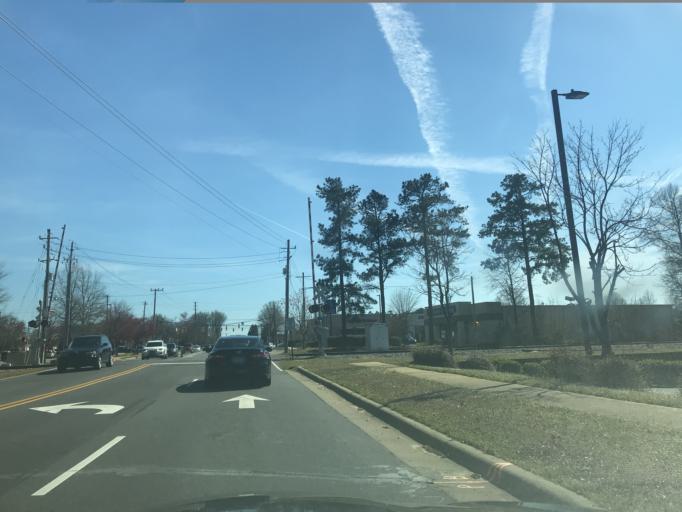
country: US
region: North Carolina
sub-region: Wake County
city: Fuquay-Varina
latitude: 35.5940
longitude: -78.7741
